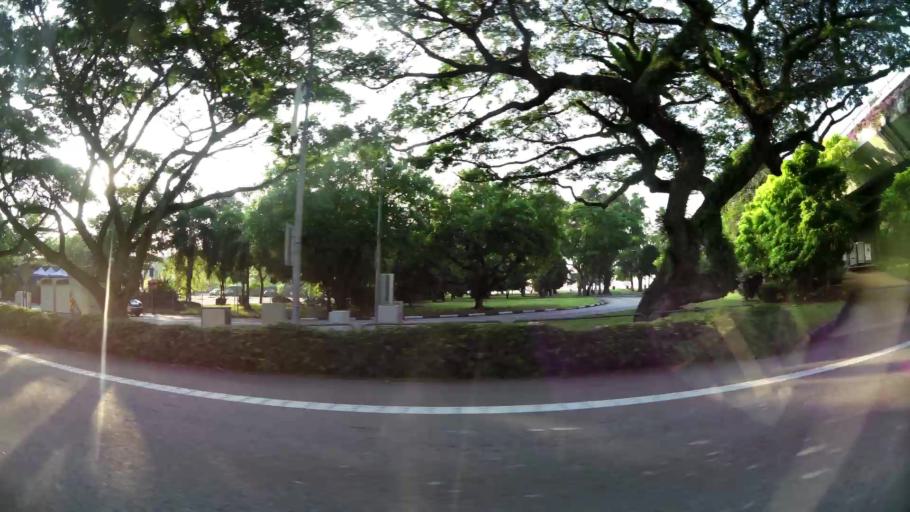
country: SG
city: Singapore
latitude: 1.2973
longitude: 103.8984
